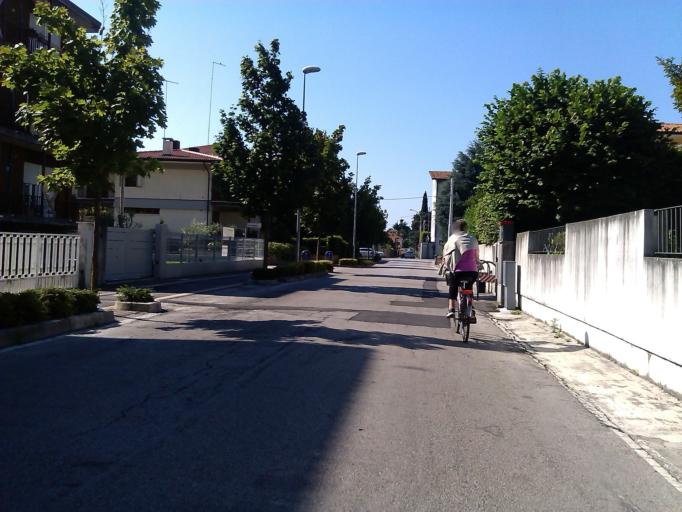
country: IT
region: Veneto
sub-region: Provincia di Vicenza
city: Bassano del Grappa
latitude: 45.7726
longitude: 11.7447
